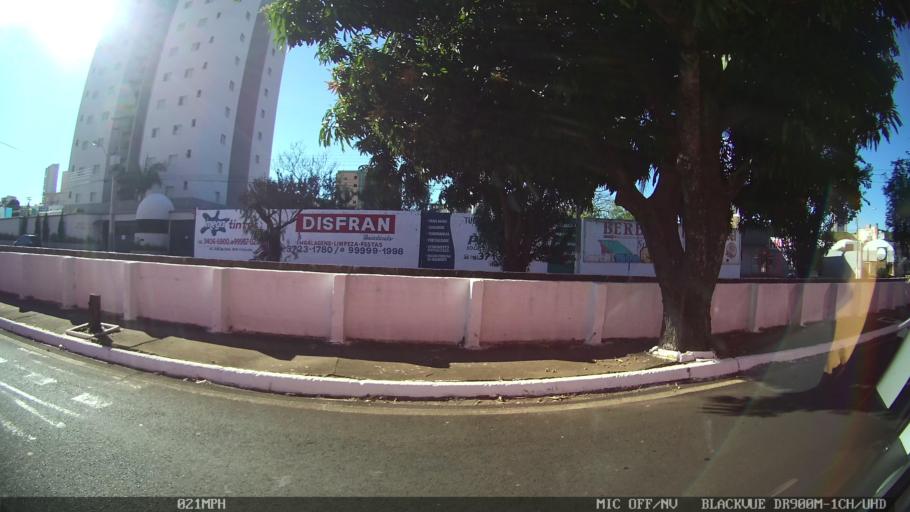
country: BR
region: Sao Paulo
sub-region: Franca
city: Franca
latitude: -20.5511
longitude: -47.4096
